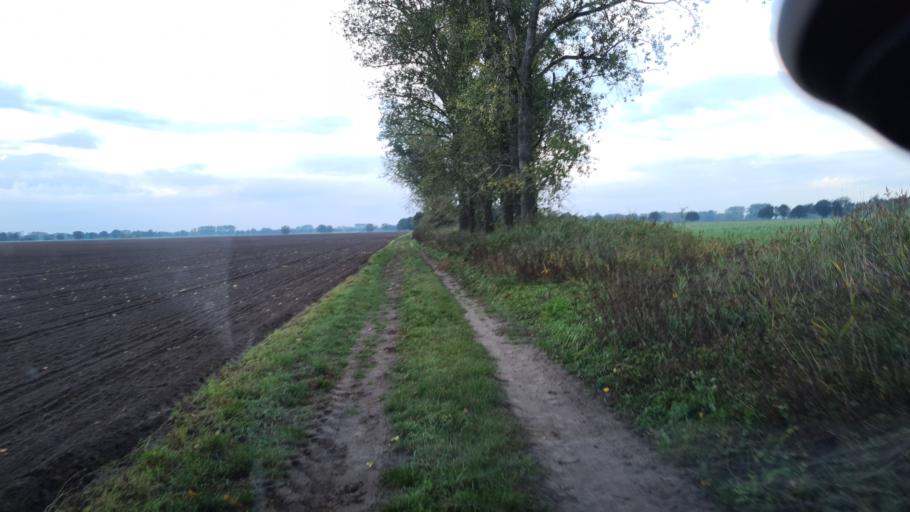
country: DE
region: Brandenburg
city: Schonewalde
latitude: 51.6886
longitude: 13.5696
